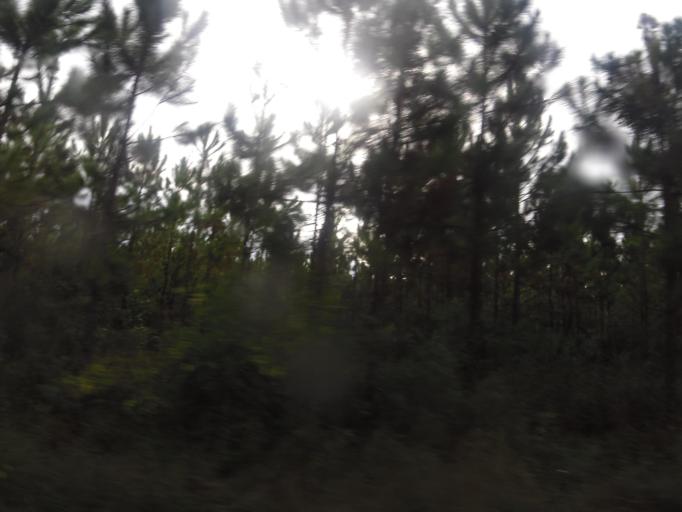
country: US
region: Florida
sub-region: Flagler County
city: Bunnell
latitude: 29.5568
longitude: -81.3309
